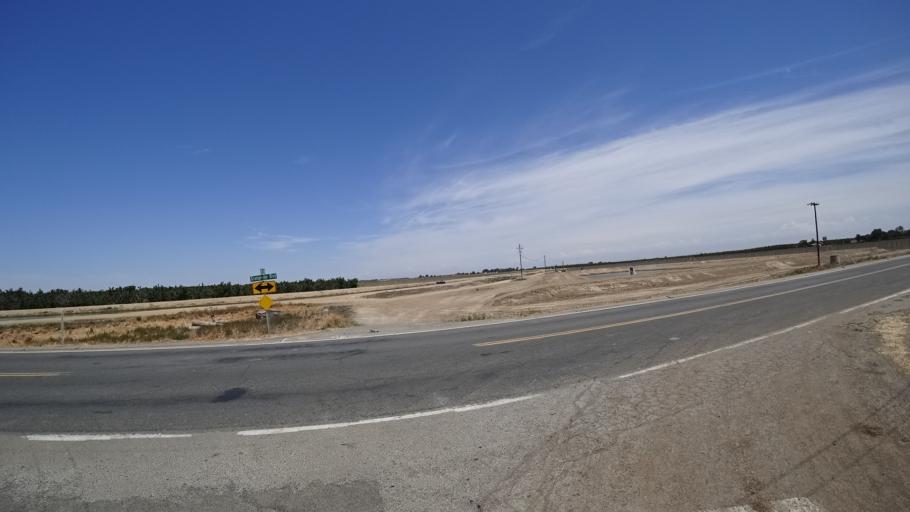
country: US
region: California
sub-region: Kings County
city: Lemoore
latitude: 36.3425
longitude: -119.7537
